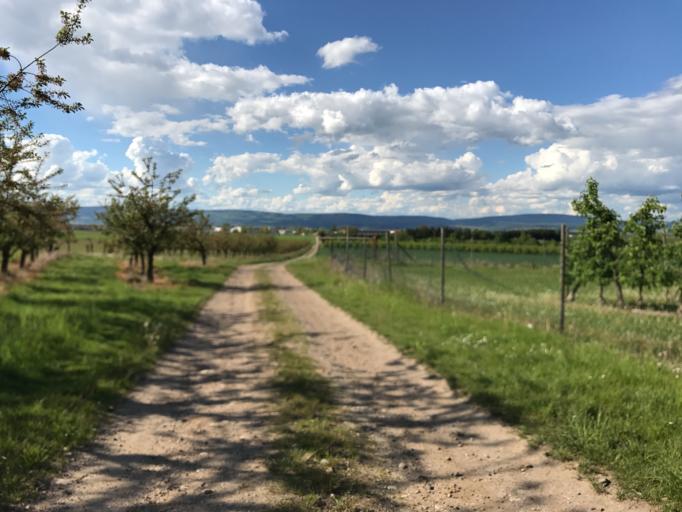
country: DE
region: Rheinland-Pfalz
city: Wackernheim
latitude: 49.9583
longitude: 8.1271
